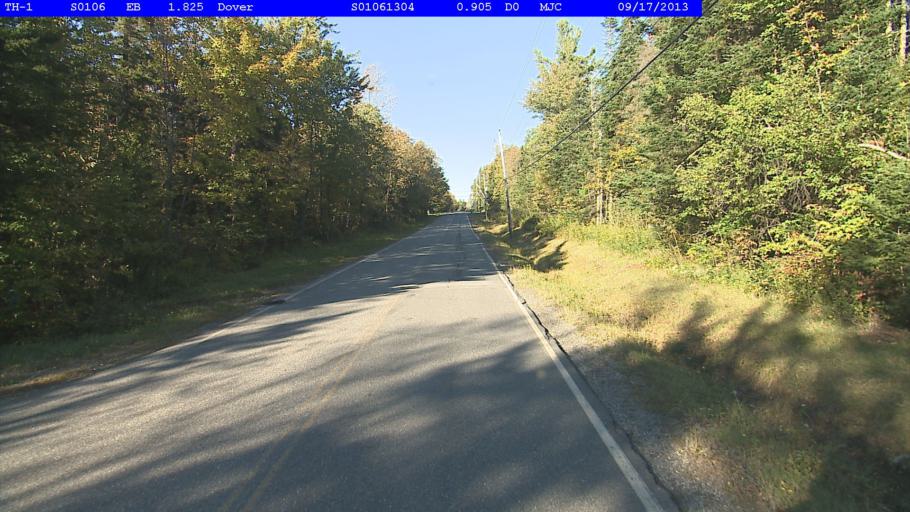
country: US
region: Vermont
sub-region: Windham County
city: Dover
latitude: 42.9295
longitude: -72.8179
